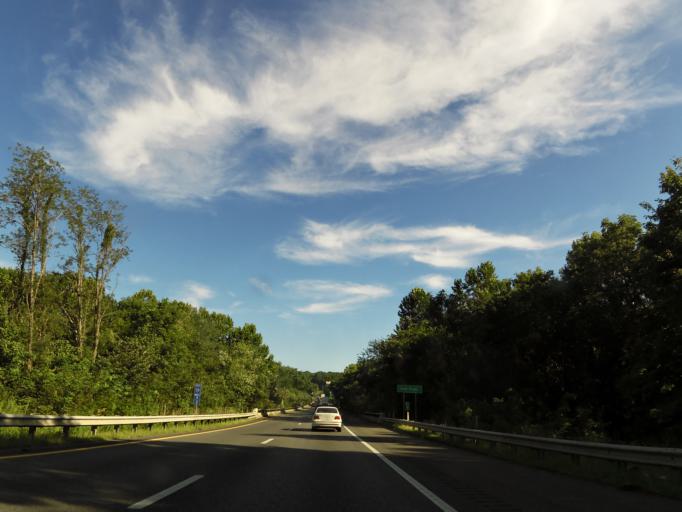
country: US
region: Tennessee
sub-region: Montgomery County
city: Clarksville
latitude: 36.5433
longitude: -87.2413
